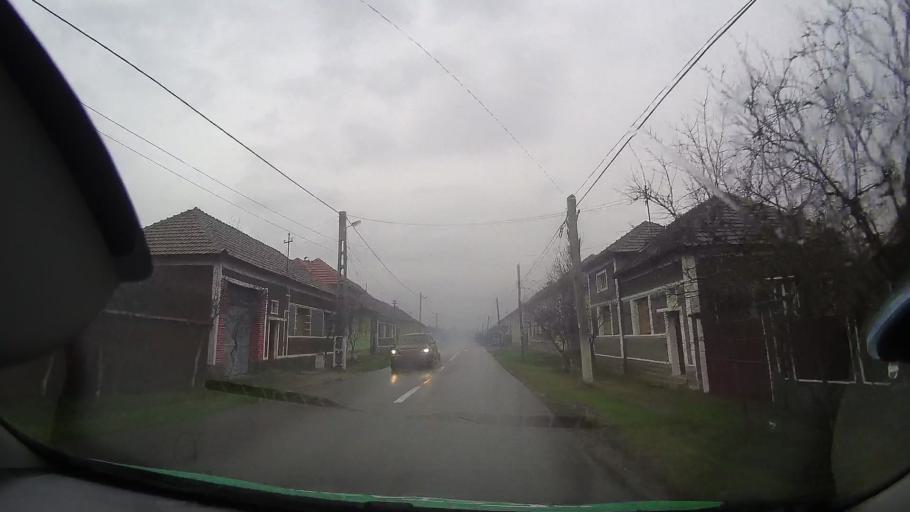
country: RO
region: Bihor
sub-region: Comuna Holod
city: Vintere
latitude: 46.7674
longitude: 22.1429
